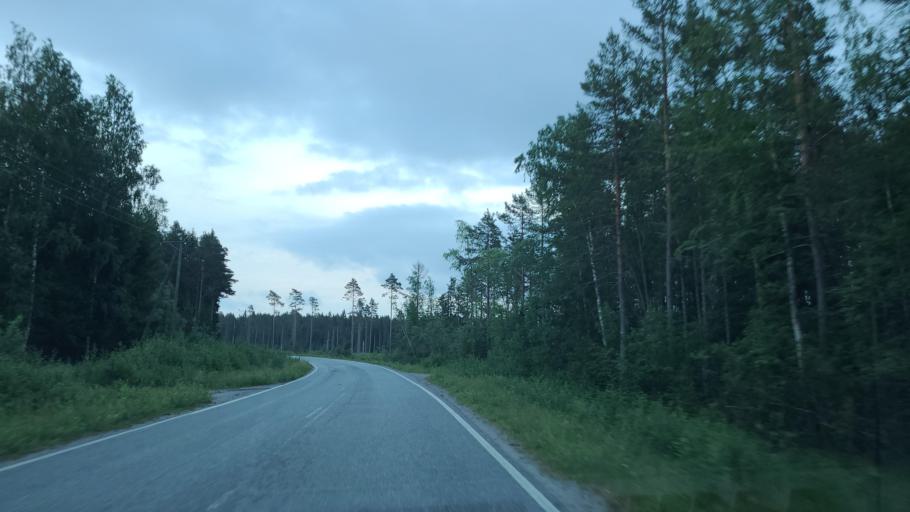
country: FI
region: Ostrobothnia
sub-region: Vaasa
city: Replot
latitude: 63.2044
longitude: 21.2698
